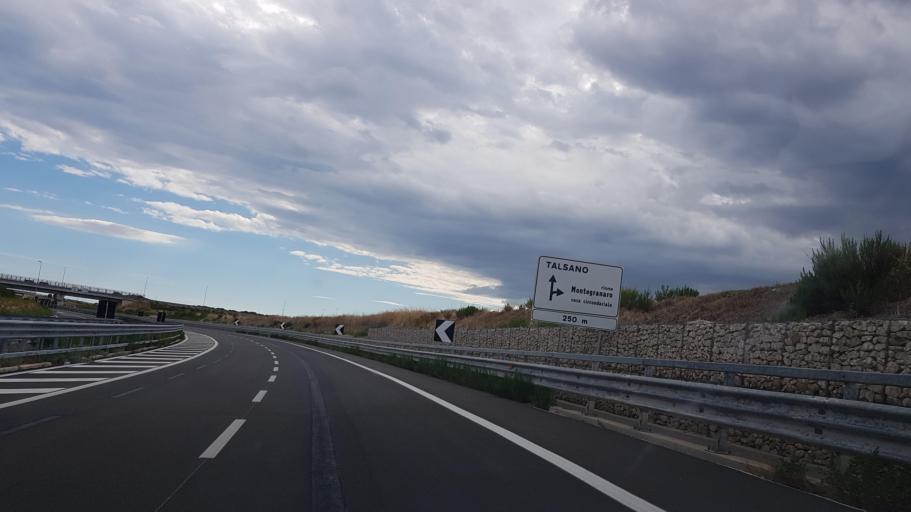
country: IT
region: Apulia
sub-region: Provincia di Taranto
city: Taranto
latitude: 40.4579
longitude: 17.2845
